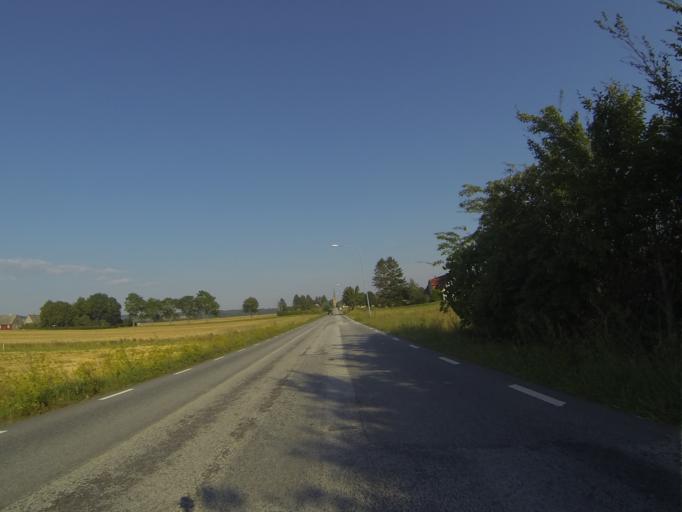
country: SE
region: Skane
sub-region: Lunds Kommun
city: Genarp
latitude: 55.6048
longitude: 13.3825
